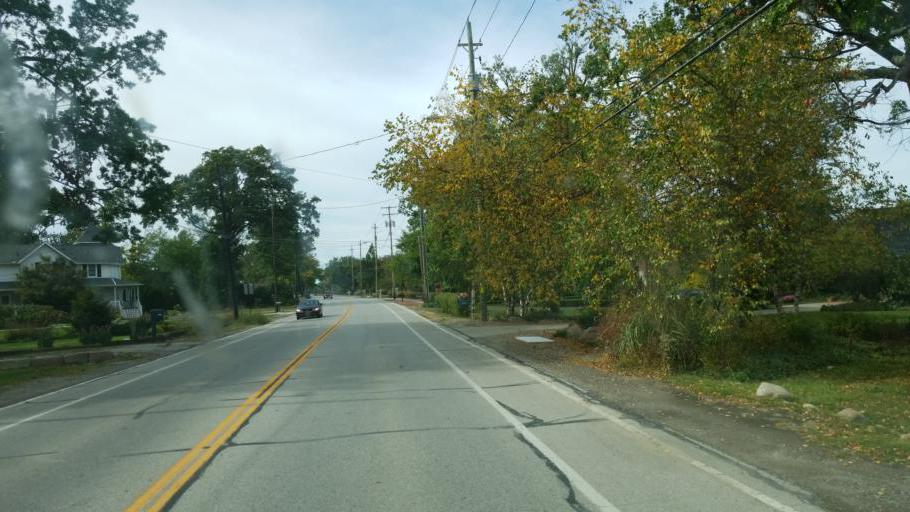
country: US
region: Ohio
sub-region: Lorain County
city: Avon Lake
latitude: 41.5086
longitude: -81.9814
